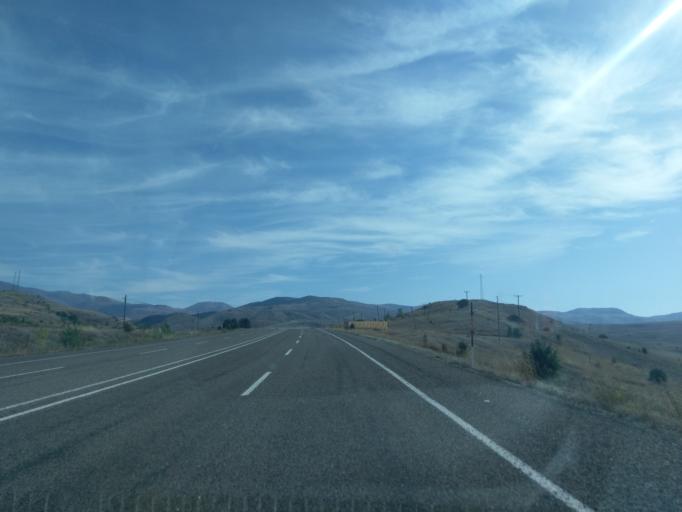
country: TR
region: Sivas
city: Imranli
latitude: 39.8355
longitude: 38.2691
